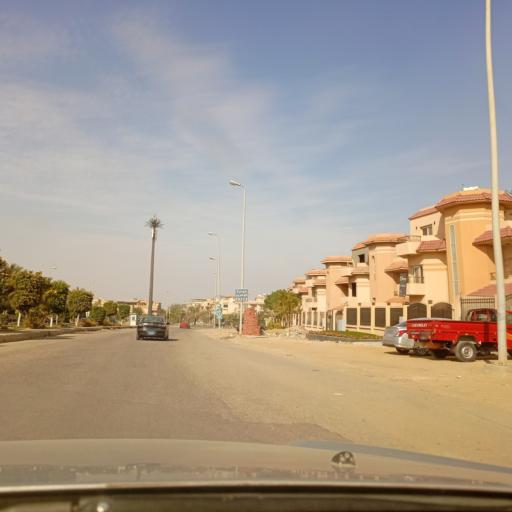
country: EG
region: Muhafazat al Qalyubiyah
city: Al Khankah
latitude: 30.0518
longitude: 31.4853
